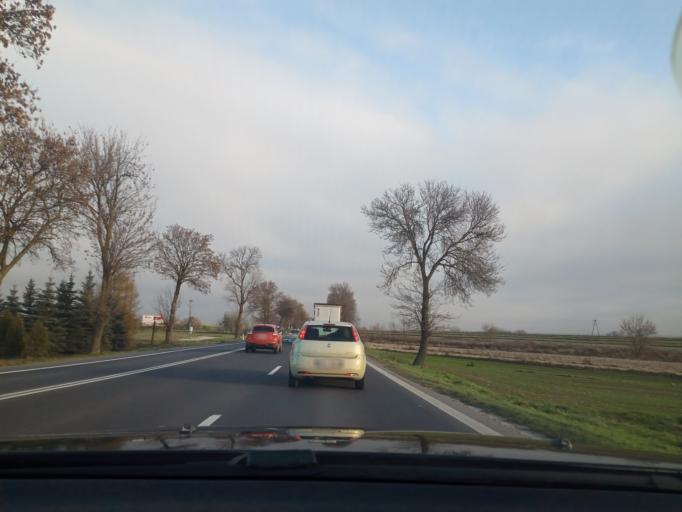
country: PL
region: Lesser Poland Voivodeship
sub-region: Powiat miechowski
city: Miechow
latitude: 50.3018
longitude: 20.0364
